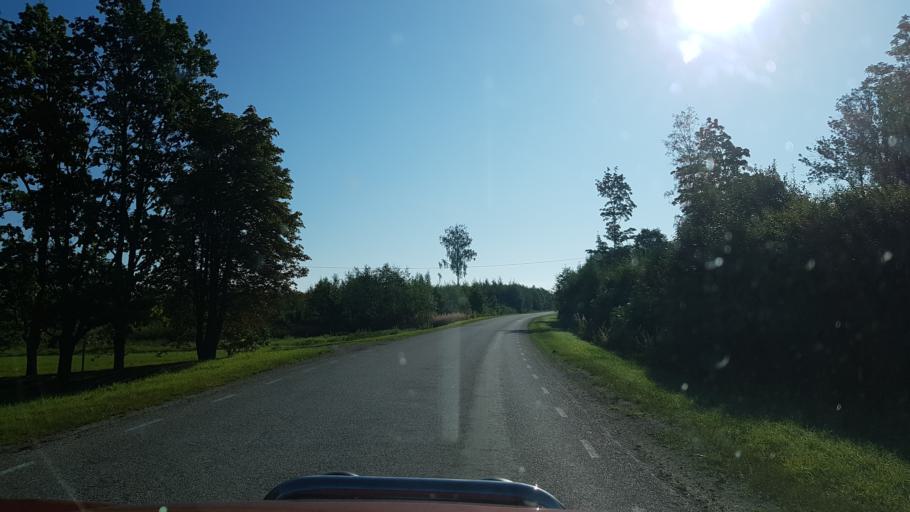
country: EE
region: Jogevamaa
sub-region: Tabivere vald
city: Tabivere
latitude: 58.6846
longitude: 26.6014
